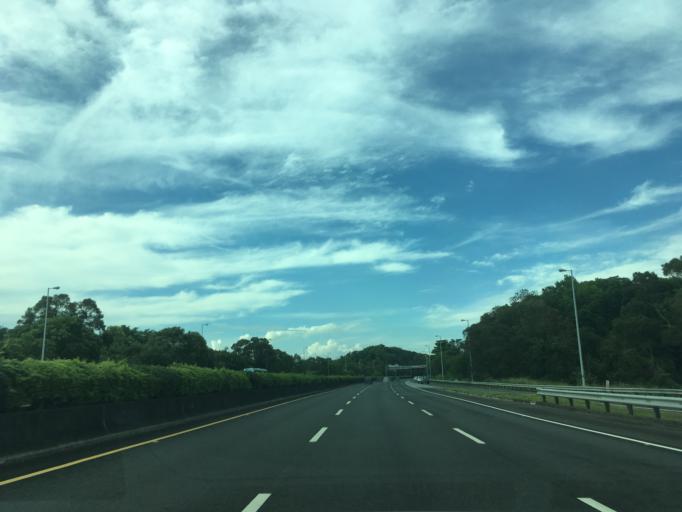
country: TW
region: Taiwan
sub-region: Chiayi
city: Jiayi Shi
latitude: 23.5225
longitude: 120.4850
